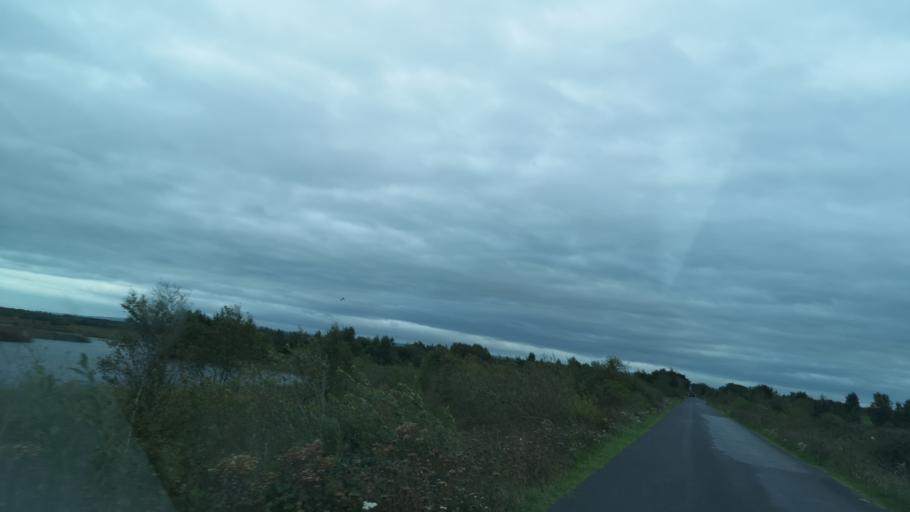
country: IE
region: Leinster
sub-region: Uibh Fhaili
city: Ferbane
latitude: 53.2184
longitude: -7.7262
